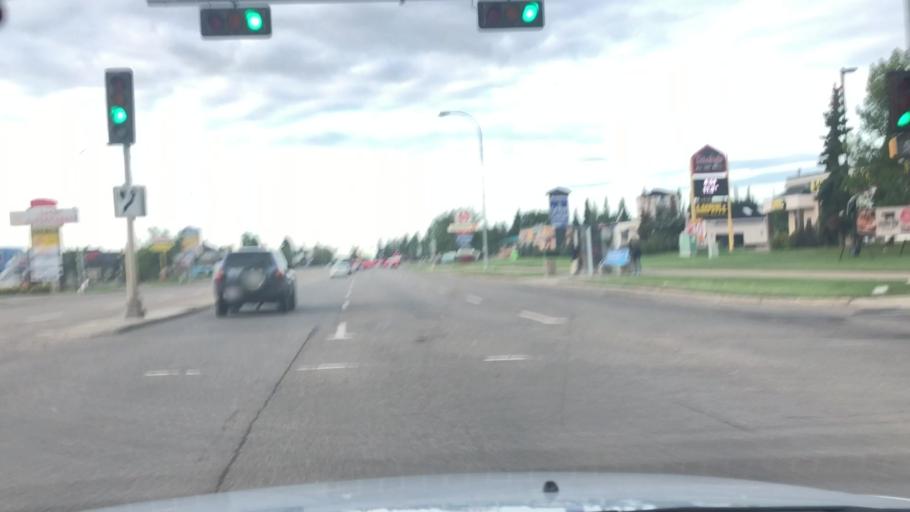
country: CA
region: Alberta
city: Edmonton
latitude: 53.6021
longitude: -113.5413
